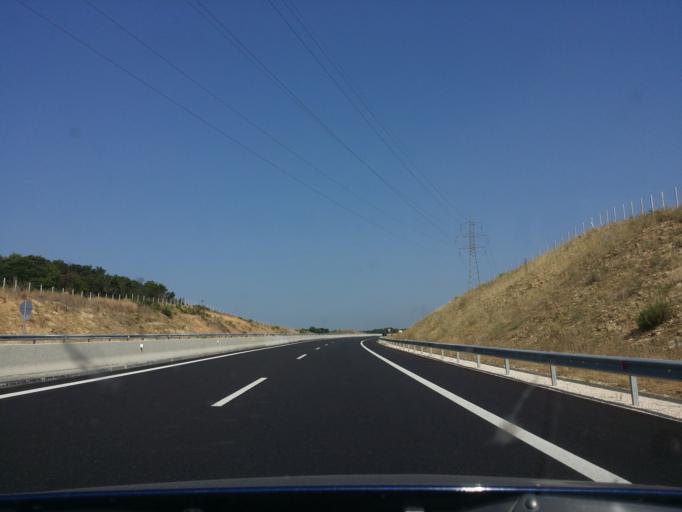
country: GR
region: West Greece
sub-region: Nomos Aitolias kai Akarnanias
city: Menidi
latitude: 39.0073
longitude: 21.1606
